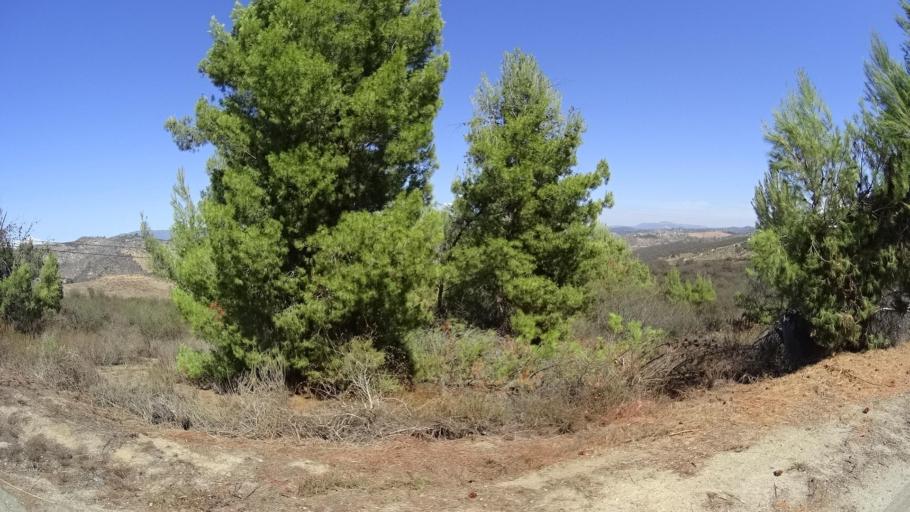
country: US
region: California
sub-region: San Diego County
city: Hidden Meadows
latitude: 33.2903
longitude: -117.1215
